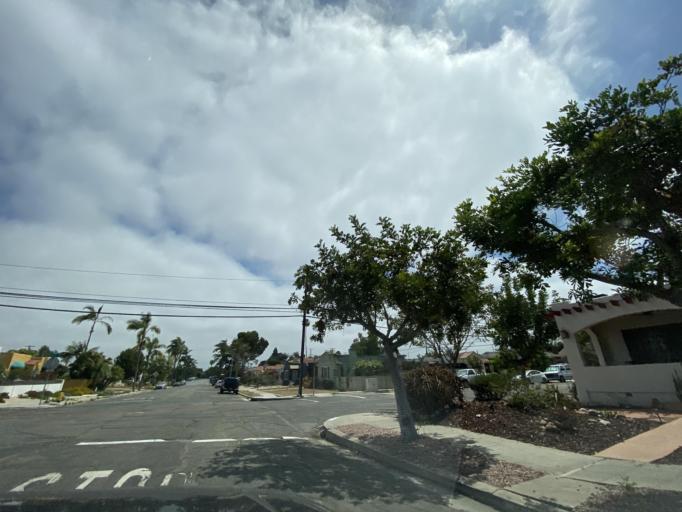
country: US
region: California
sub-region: San Diego County
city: San Diego
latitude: 32.7440
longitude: -117.1229
